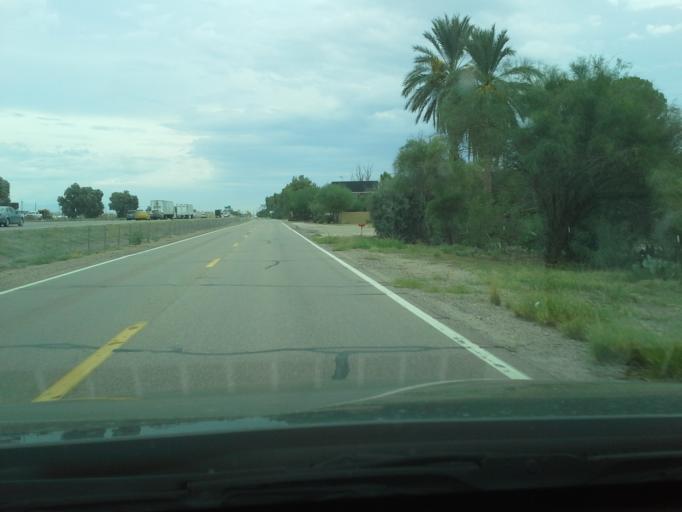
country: US
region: Arizona
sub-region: Pima County
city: Marana
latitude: 32.4151
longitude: -111.1517
